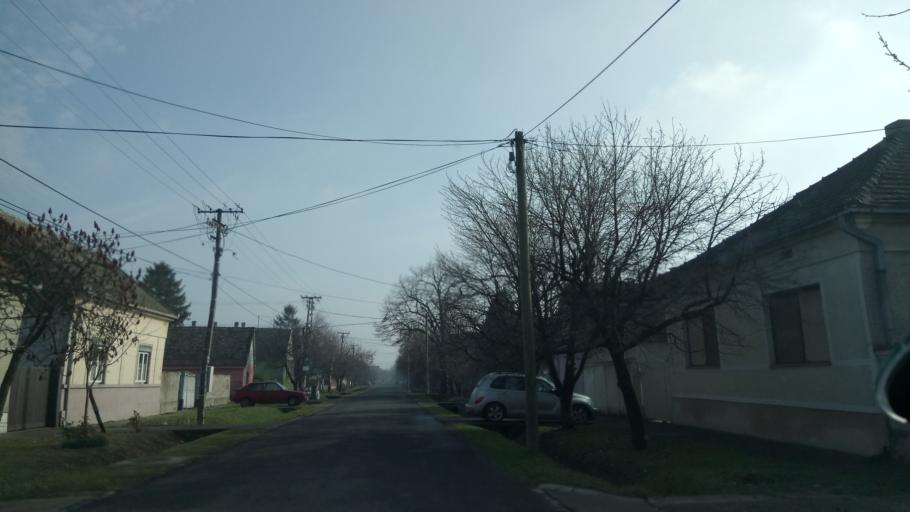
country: RS
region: Autonomna Pokrajina Vojvodina
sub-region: Sremski Okrug
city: Stara Pazova
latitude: 44.9813
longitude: 20.1636
